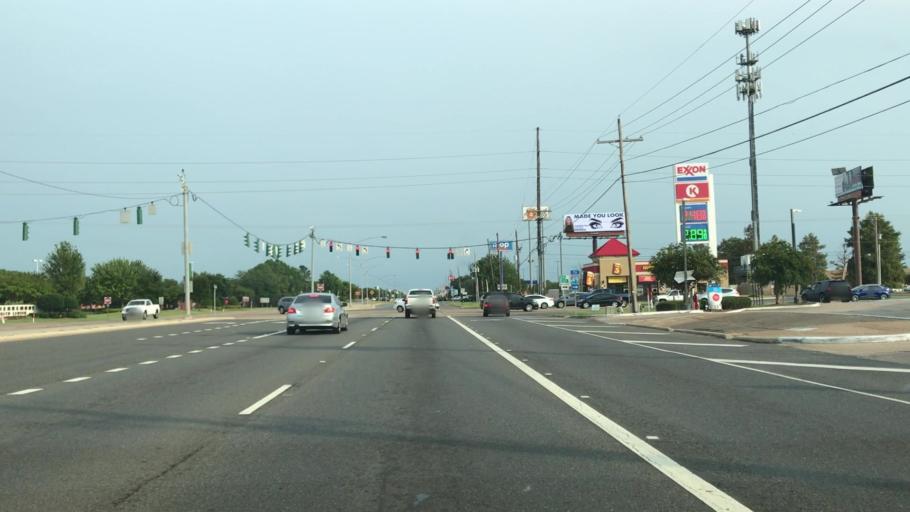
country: US
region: Louisiana
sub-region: Bossier Parish
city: Bossier City
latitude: 32.4324
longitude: -93.7124
